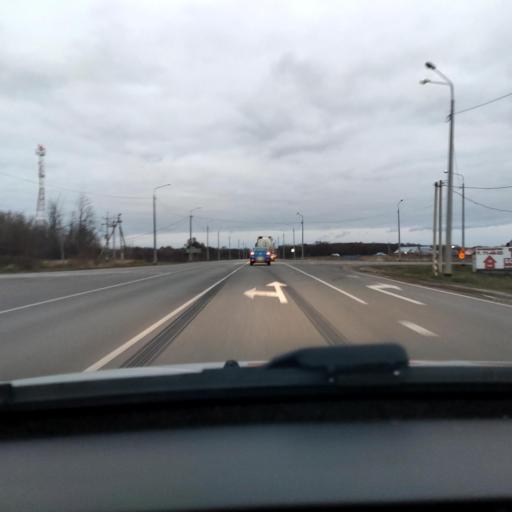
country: RU
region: Lipetsk
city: Borinskoye
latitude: 52.4623
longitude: 39.3289
